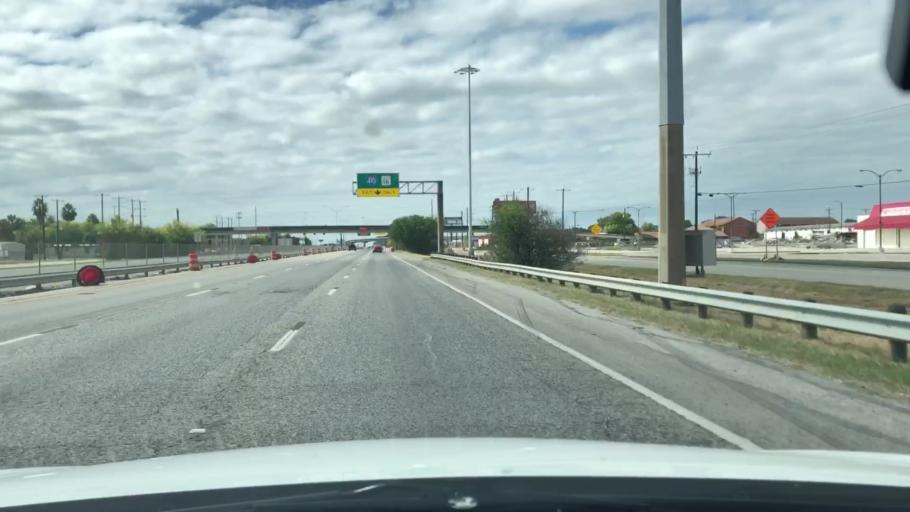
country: US
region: Texas
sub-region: Bexar County
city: Lackland Air Force Base
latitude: 29.4003
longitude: -98.6382
